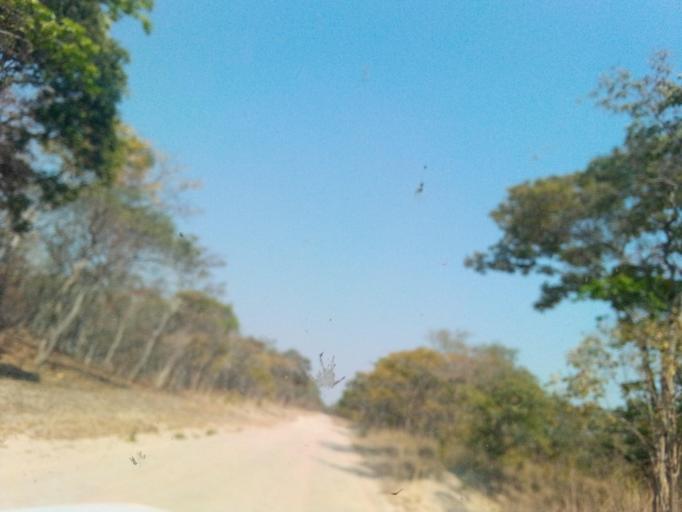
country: ZM
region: Northern
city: Mpika
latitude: -12.2264
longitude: 30.9036
